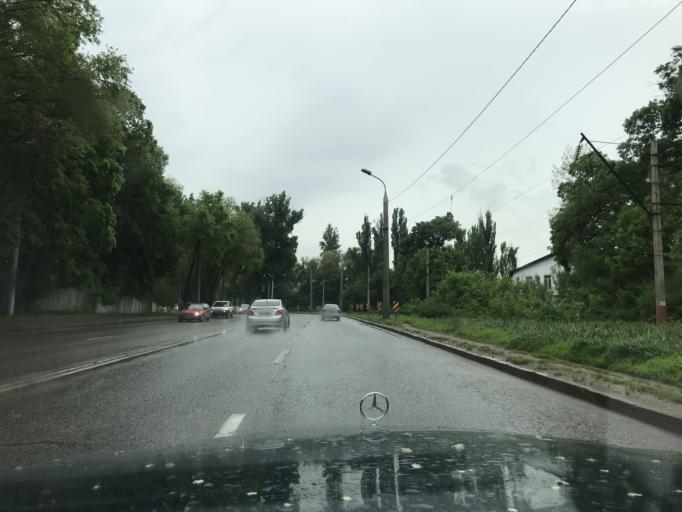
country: KZ
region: Almaty Qalasy
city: Almaty
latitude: 43.2934
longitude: 76.9475
